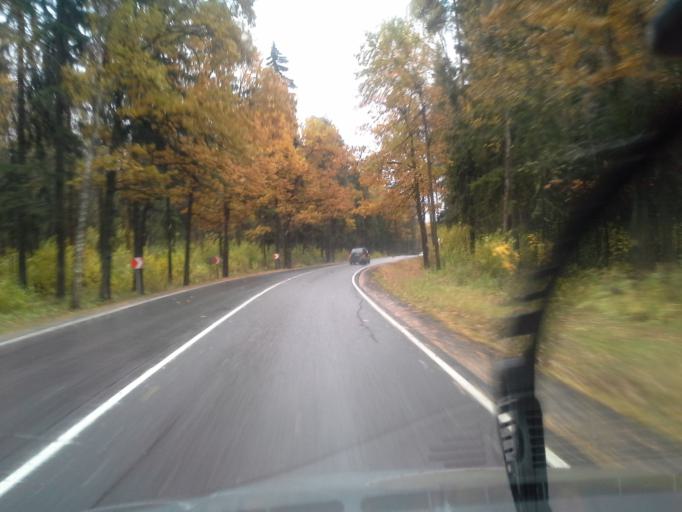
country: RU
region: Moskovskaya
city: Odintsovo
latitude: 55.7058
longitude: 37.2236
